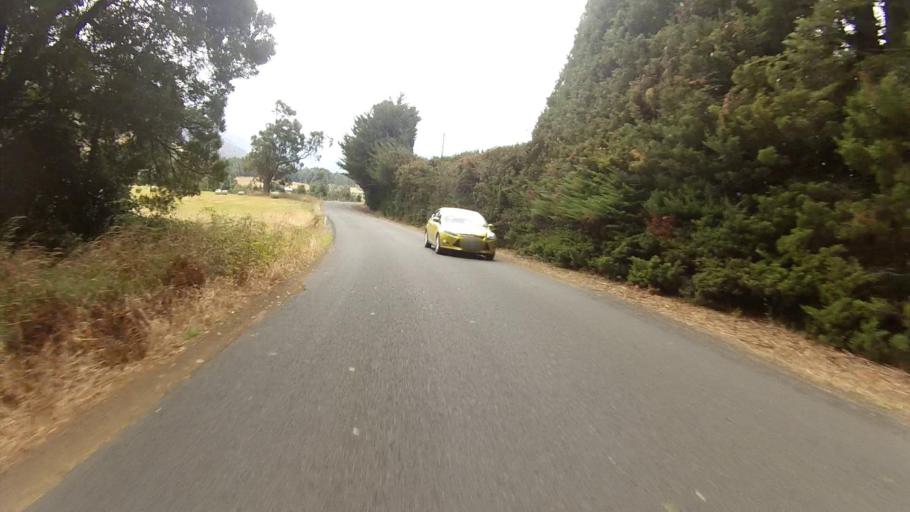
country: AU
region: Tasmania
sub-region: Huon Valley
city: Huonville
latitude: -42.9867
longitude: 147.0603
